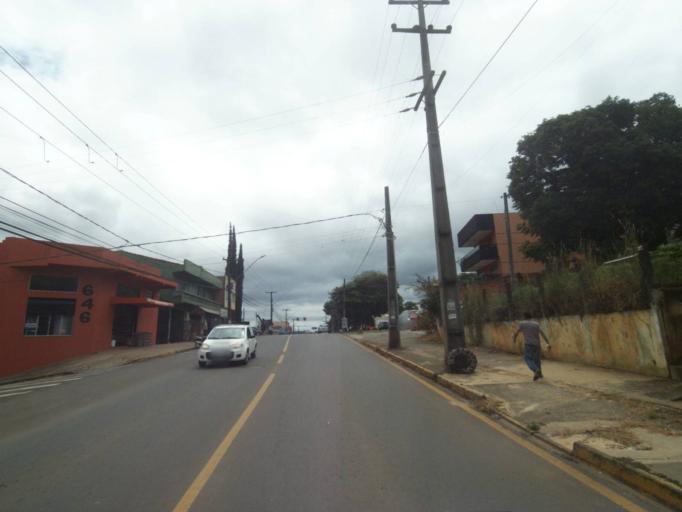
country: BR
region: Parana
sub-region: Telemaco Borba
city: Telemaco Borba
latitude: -24.3327
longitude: -50.6357
